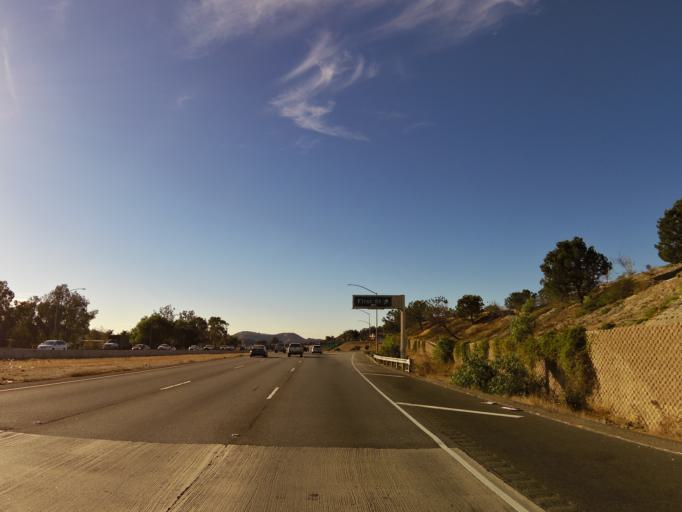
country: US
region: California
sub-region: Ventura County
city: Simi Valley
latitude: 34.2824
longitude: -118.7730
